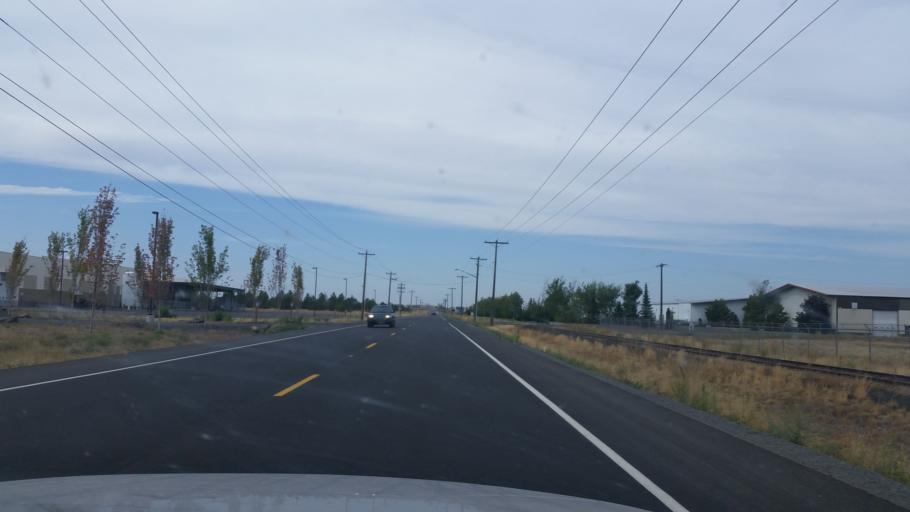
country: US
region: Washington
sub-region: Spokane County
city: Airway Heights
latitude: 47.6283
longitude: -117.5865
